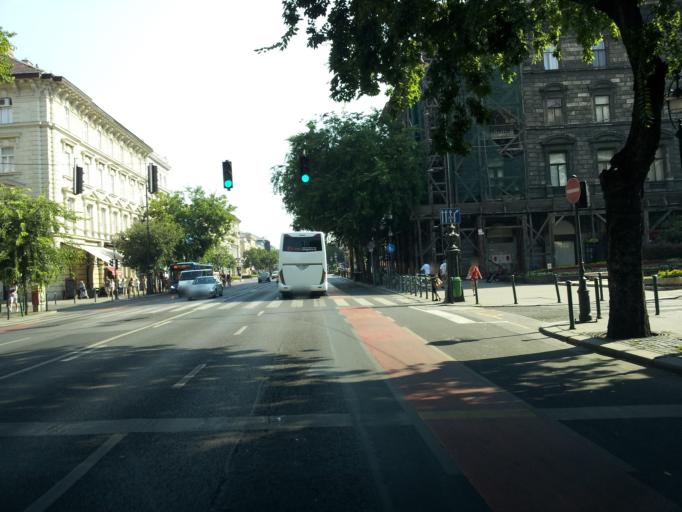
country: HU
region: Budapest
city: Budapest VI. keruelet
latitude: 47.5044
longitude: 19.0620
